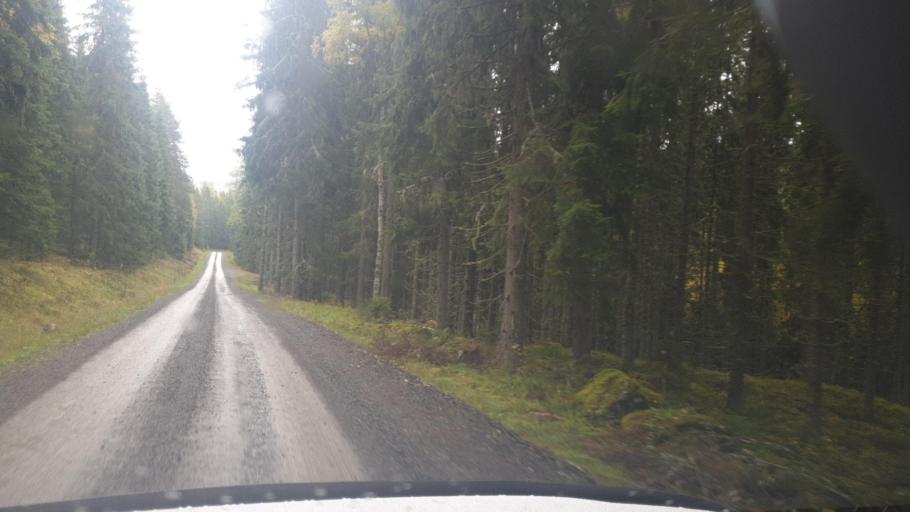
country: SE
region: Vaermland
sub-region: Sunne Kommun
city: Sunne
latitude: 59.8598
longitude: 12.8378
